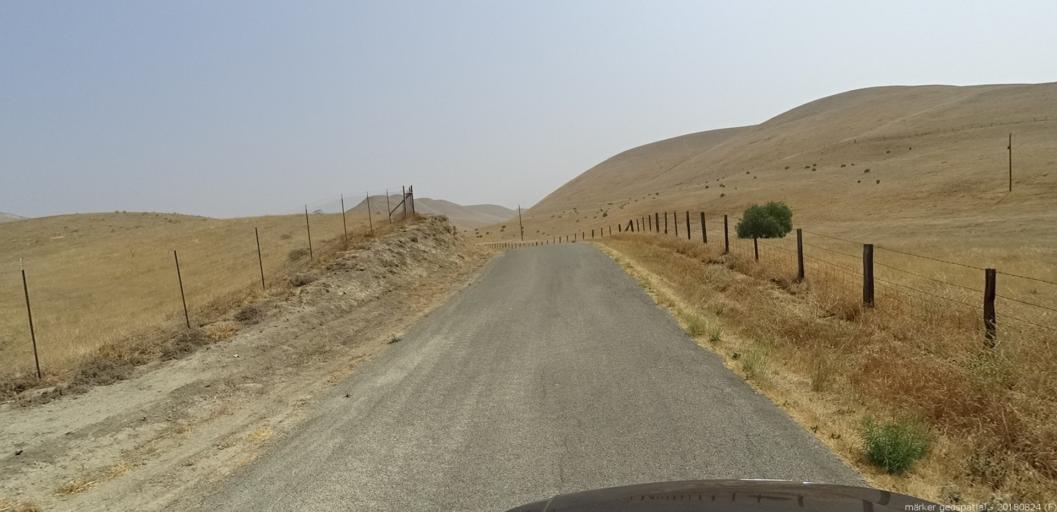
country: US
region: California
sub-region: Monterey County
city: King City
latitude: 36.1982
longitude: -121.0229
